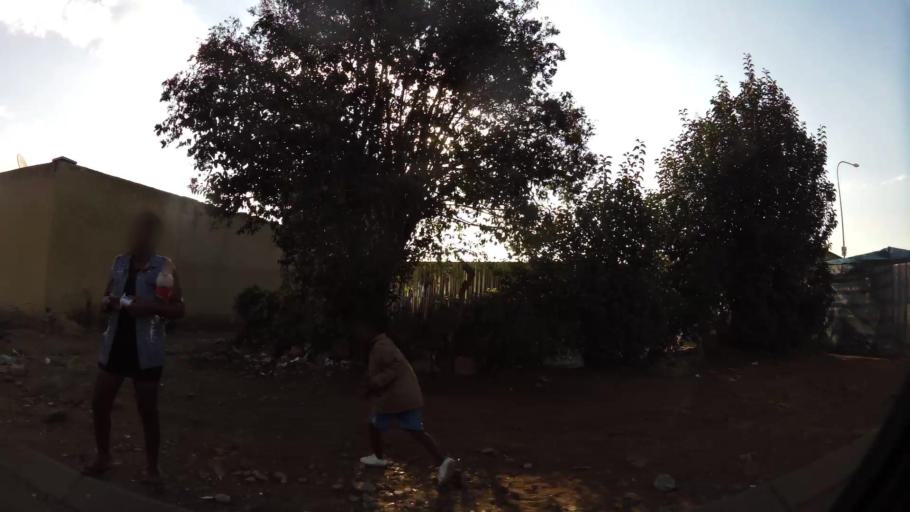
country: ZA
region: Gauteng
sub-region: City of Johannesburg Metropolitan Municipality
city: Soweto
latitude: -26.2274
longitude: 27.8955
